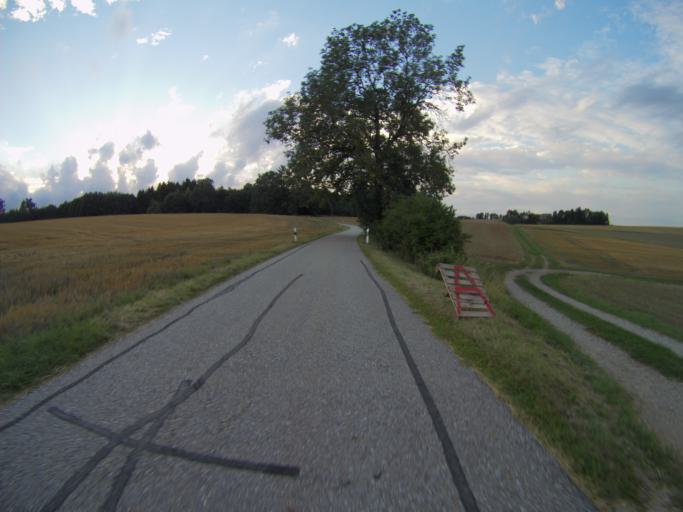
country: DE
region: Bavaria
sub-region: Upper Bavaria
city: Freising
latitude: 48.4306
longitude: 11.7077
